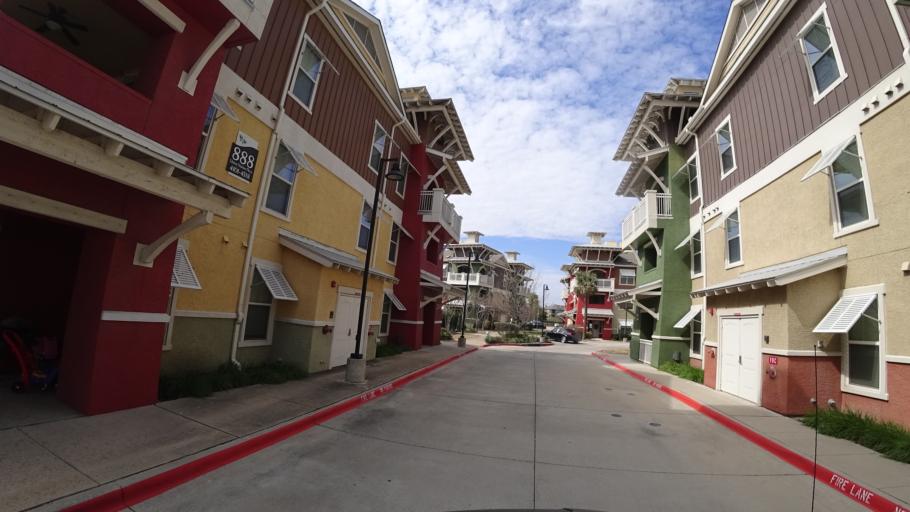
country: US
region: Texas
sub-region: Denton County
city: Lewisville
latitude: 33.0065
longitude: -96.9618
